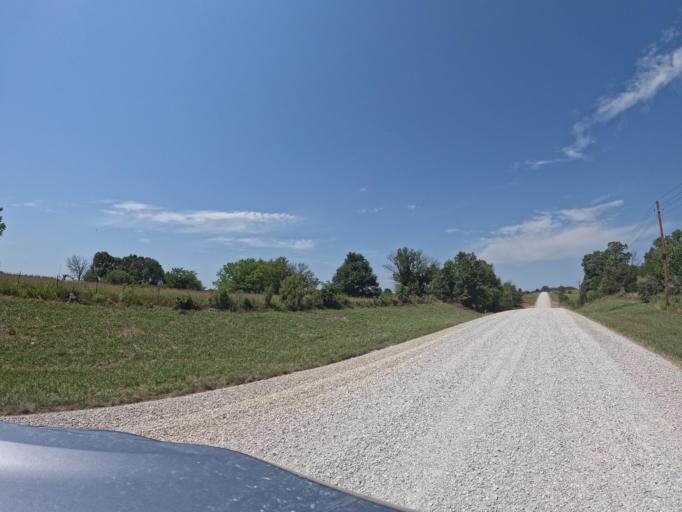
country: US
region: Iowa
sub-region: Henry County
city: Mount Pleasant
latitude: 40.8943
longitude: -91.6890
